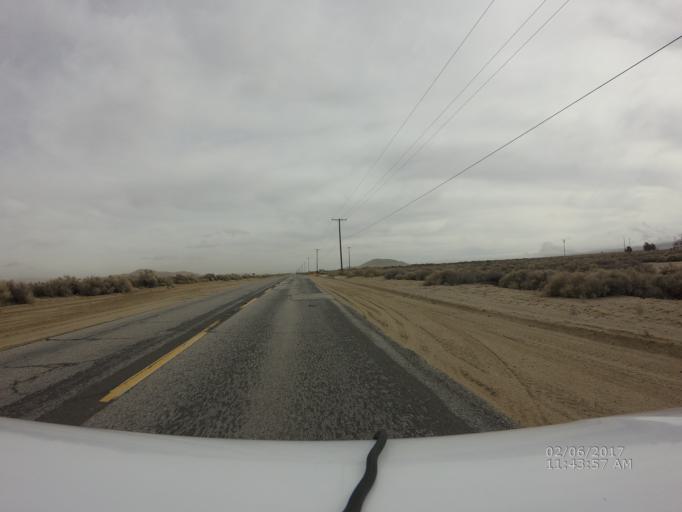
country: US
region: California
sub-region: Los Angeles County
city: Lake Los Angeles
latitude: 34.6019
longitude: -117.6862
